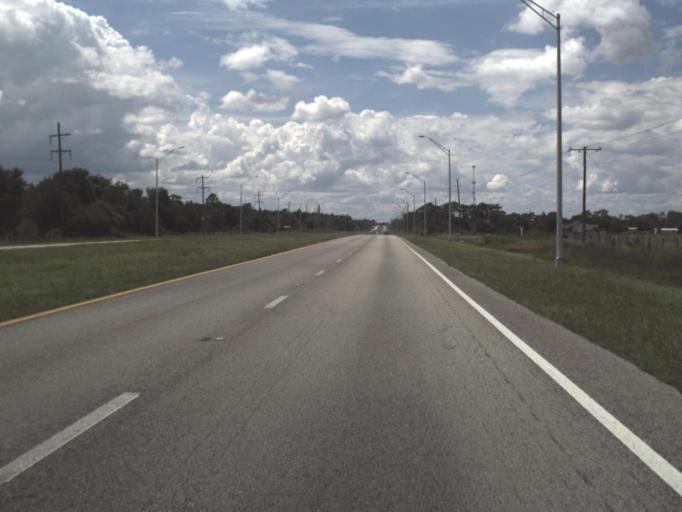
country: US
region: Florida
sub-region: Polk County
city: Babson Park
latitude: 27.8780
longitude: -81.4126
